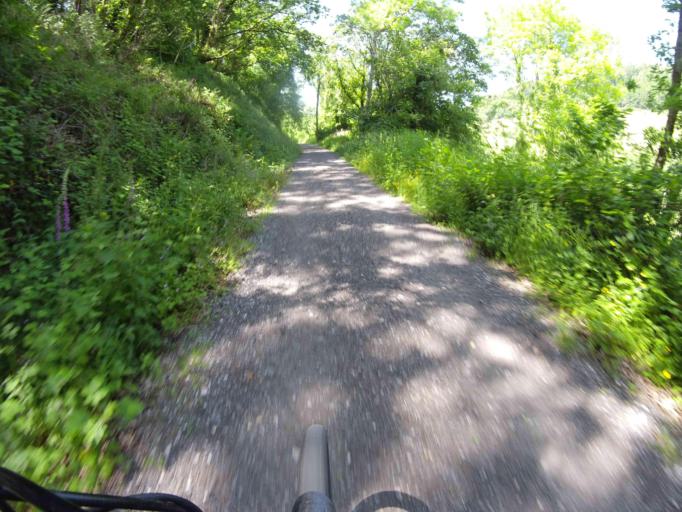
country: GB
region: England
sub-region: Devon
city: Bovey Tracey
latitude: 50.6275
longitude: -3.7189
